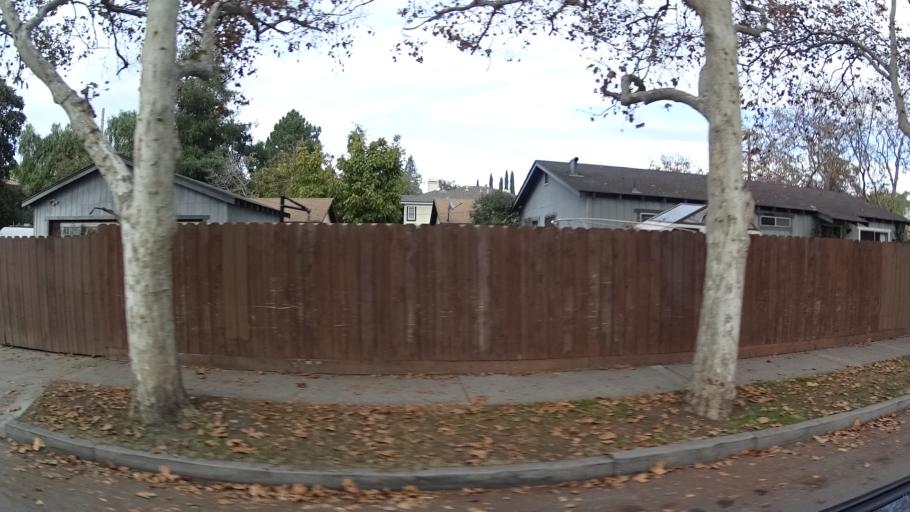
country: US
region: California
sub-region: Santa Clara County
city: Buena Vista
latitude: 37.3278
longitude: -121.9221
